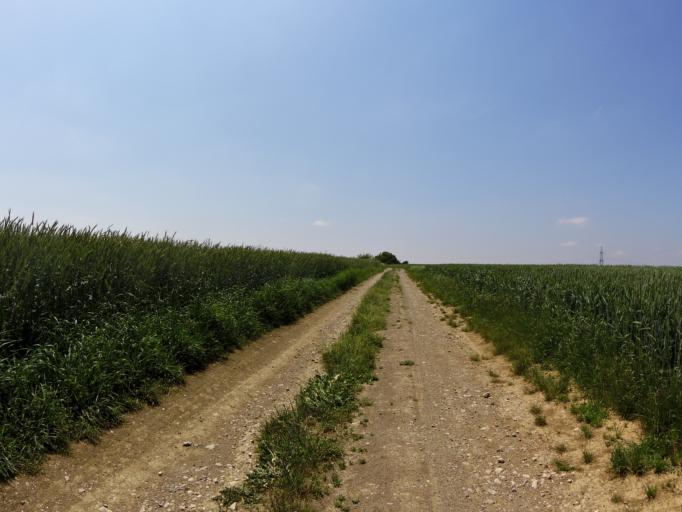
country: DE
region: Bavaria
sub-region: Regierungsbezirk Unterfranken
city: Kleinrinderfeld
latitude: 49.7137
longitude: 9.8516
